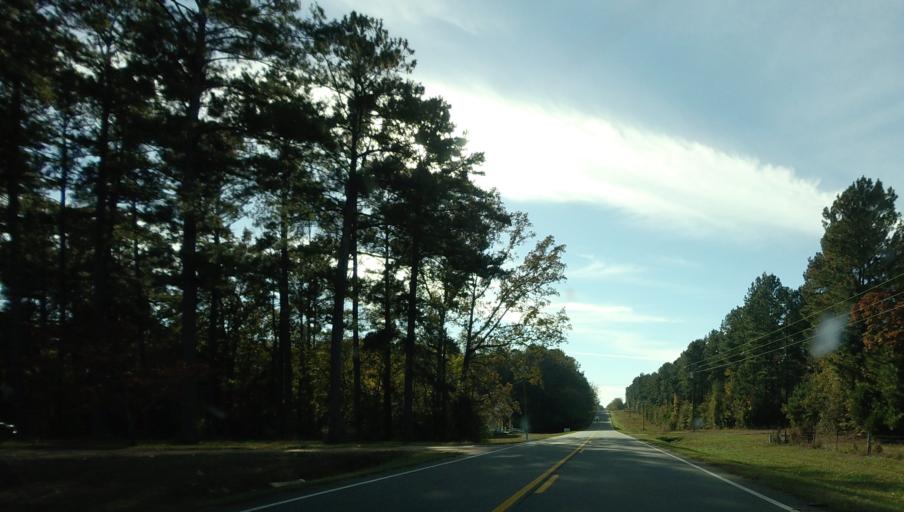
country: US
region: Georgia
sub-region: Talbot County
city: Talbotton
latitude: 32.6957
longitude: -84.4527
